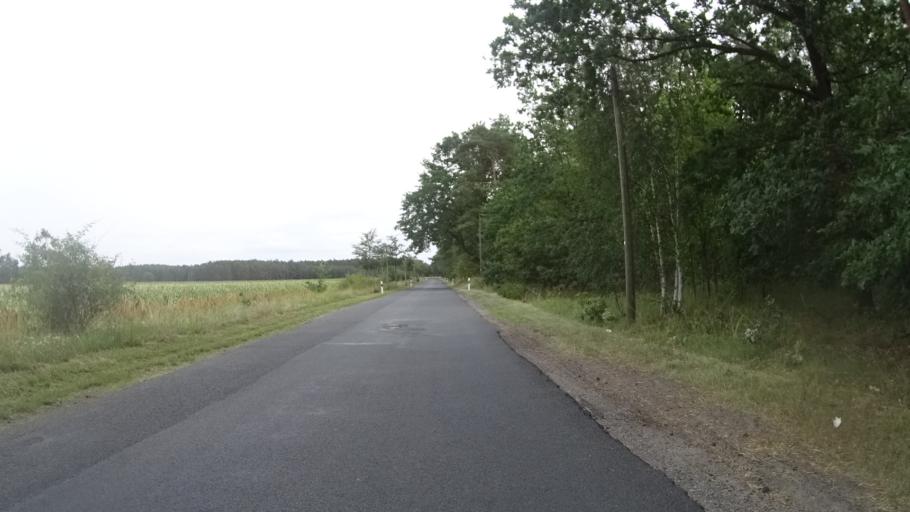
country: DE
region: Brandenburg
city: Beelitz
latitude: 52.1849
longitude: 12.9512
